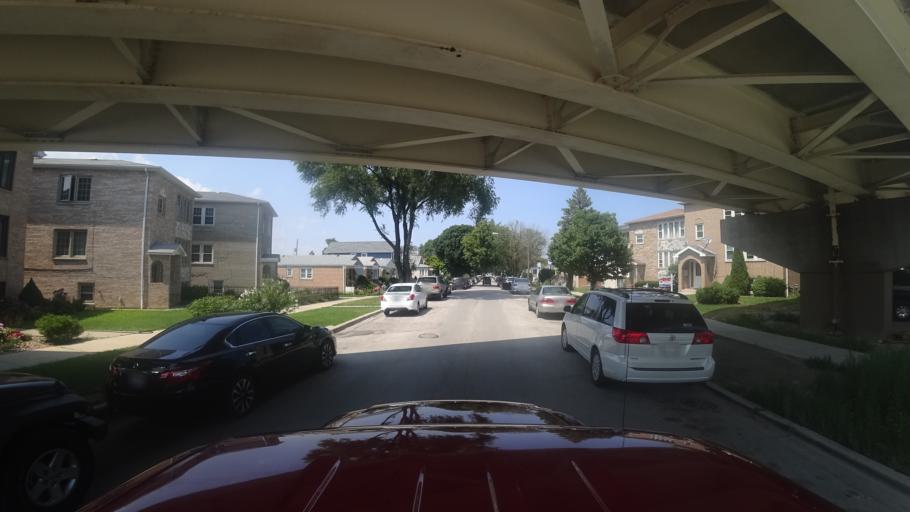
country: US
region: Illinois
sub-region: Cook County
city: Cicero
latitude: 41.7969
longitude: -87.7318
